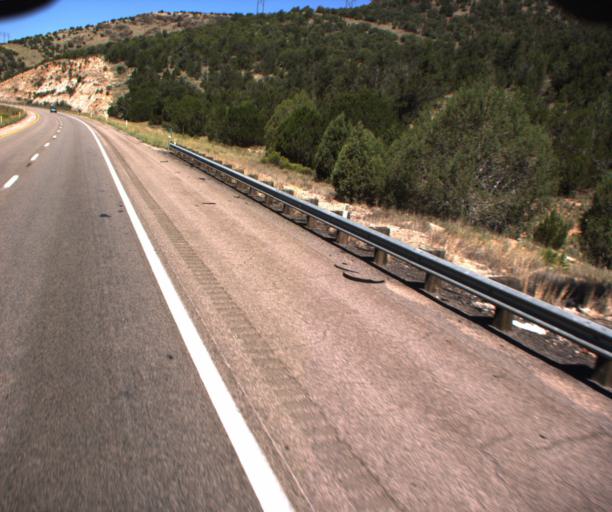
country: US
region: Arizona
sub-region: Mohave County
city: Peach Springs
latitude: 35.2873
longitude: -113.1073
